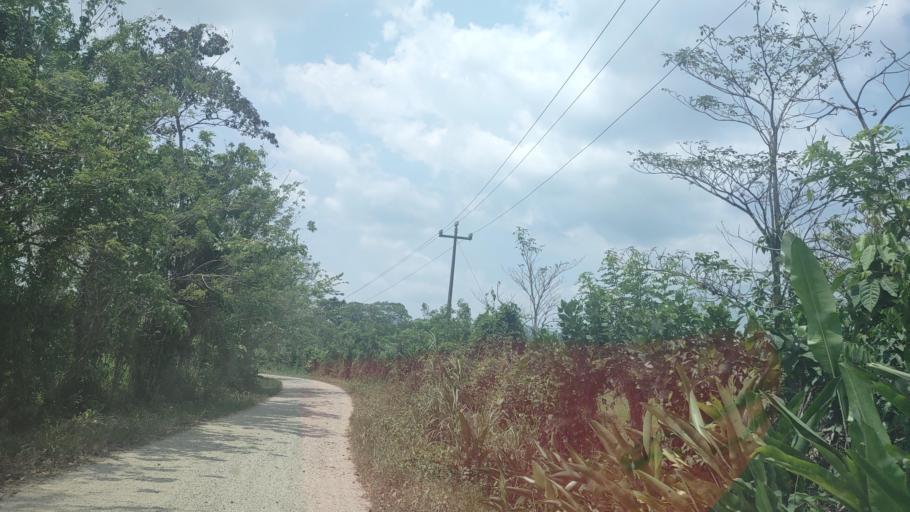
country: MX
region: Chiapas
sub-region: Tecpatan
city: Raudales Malpaso
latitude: 17.2714
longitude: -93.8719
